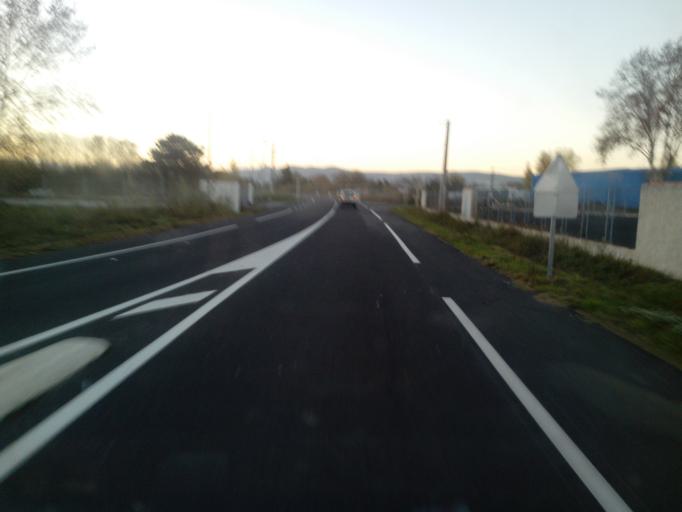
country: FR
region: Languedoc-Roussillon
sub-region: Departement des Pyrenees-Orientales
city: Rivesaltes
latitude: 42.7706
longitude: 2.8996
